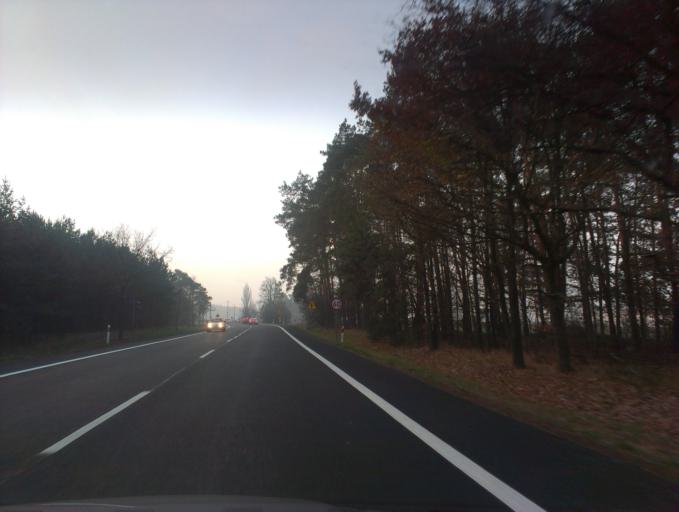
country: PL
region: Greater Poland Voivodeship
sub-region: Powiat obornicki
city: Rogozno
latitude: 52.8053
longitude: 16.9770
